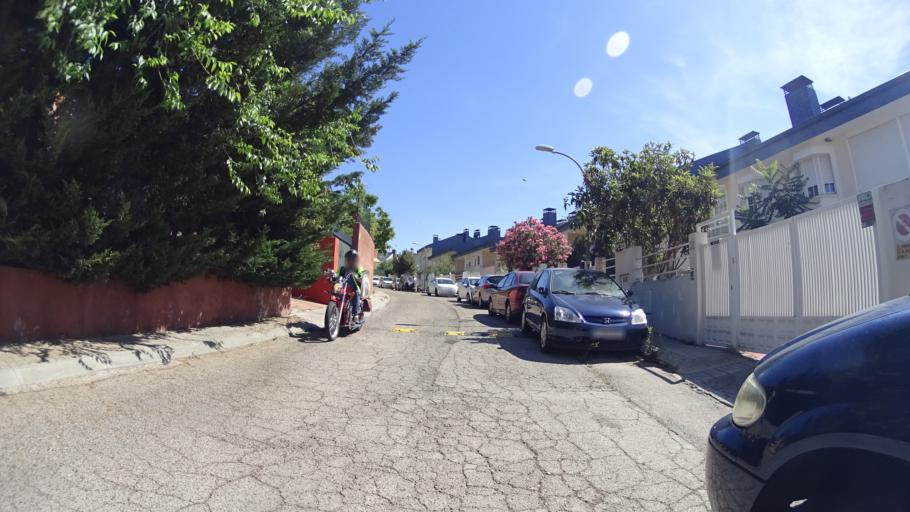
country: ES
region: Madrid
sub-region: Provincia de Madrid
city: Torrelodones
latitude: 40.5945
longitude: -3.9581
